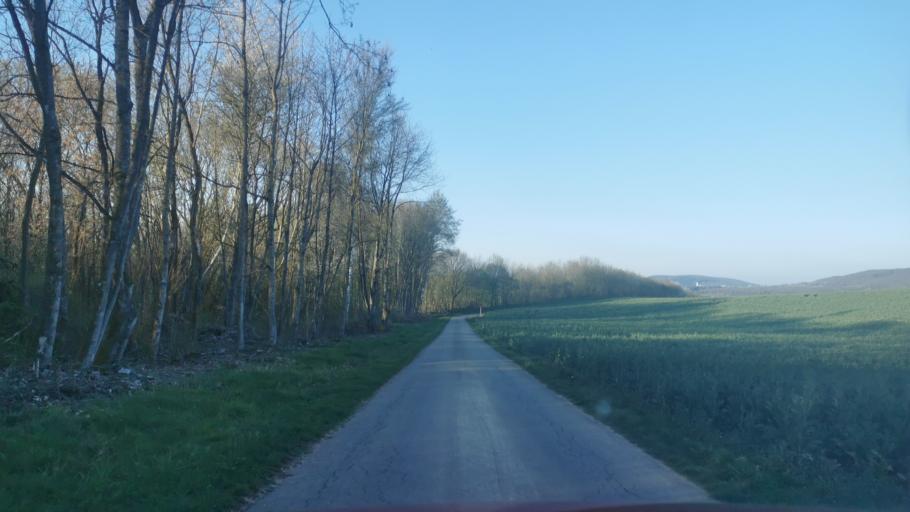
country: DE
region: Rheinland-Pfalz
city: Hetzerath
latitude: 49.8737
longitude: 6.8326
